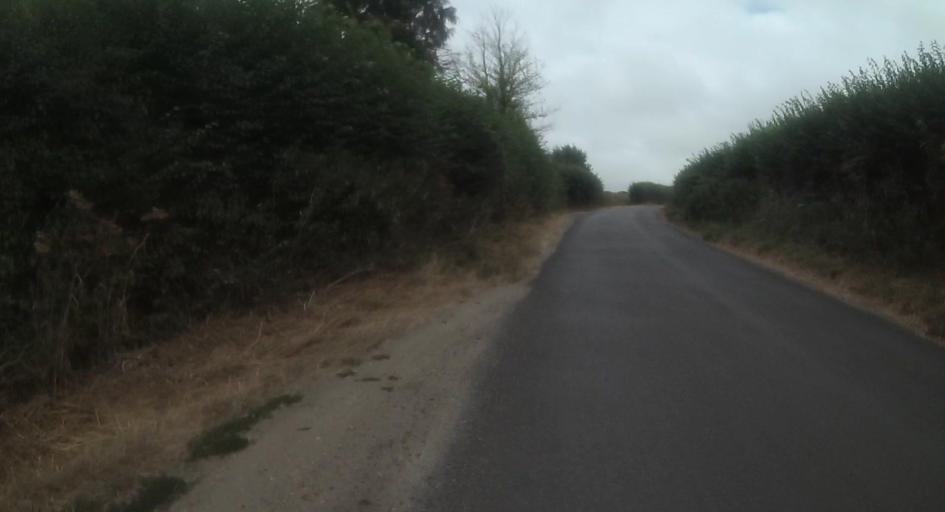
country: GB
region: England
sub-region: Dorset
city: Bovington Camp
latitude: 50.7107
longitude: -2.2927
